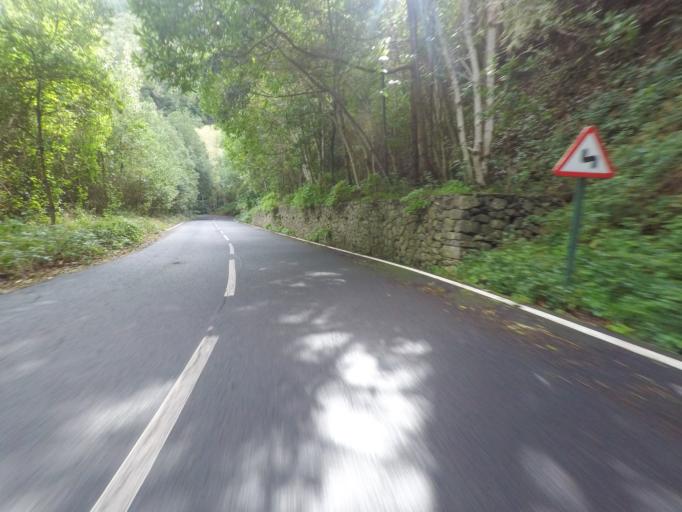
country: ES
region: Canary Islands
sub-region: Provincia de Santa Cruz de Tenerife
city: Hermigua
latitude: 28.1280
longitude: -17.2075
